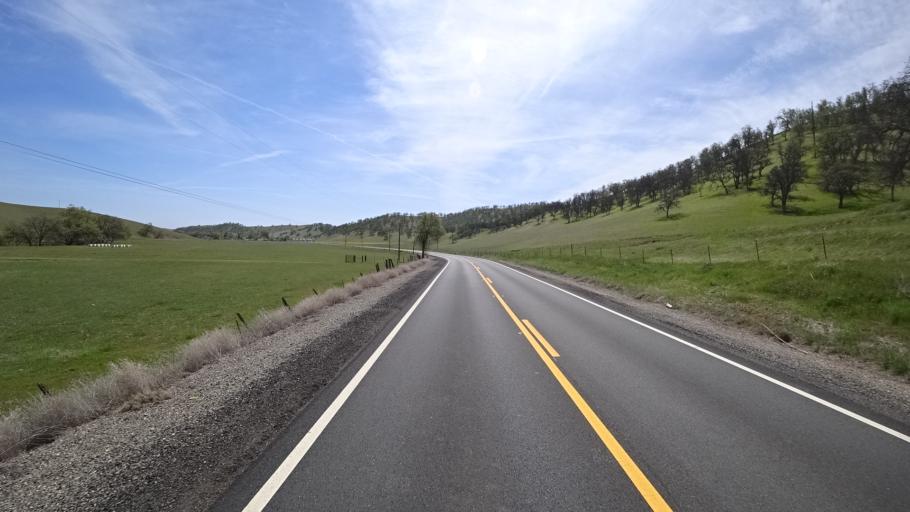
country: US
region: California
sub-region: Glenn County
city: Willows
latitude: 39.5931
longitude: -122.4610
